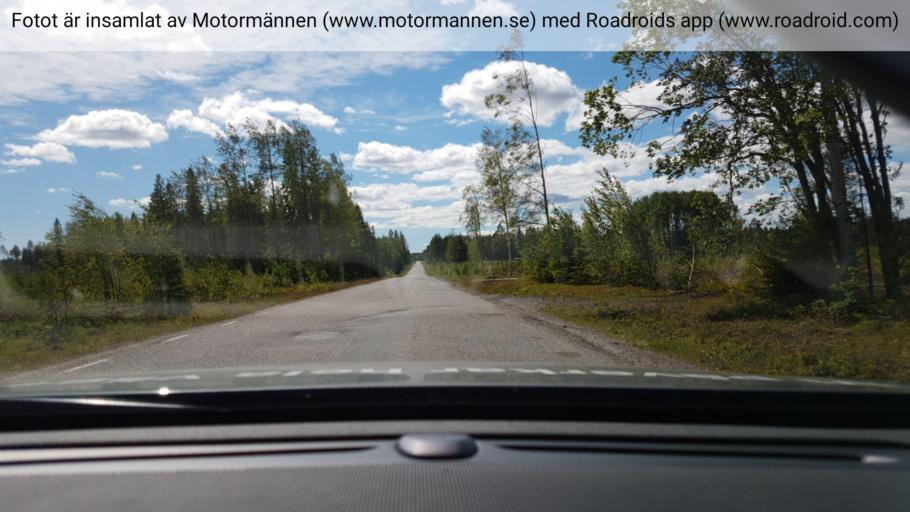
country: SE
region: Vaesterbotten
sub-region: Skelleftea Kommun
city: Burea
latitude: 64.4215
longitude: 21.3528
